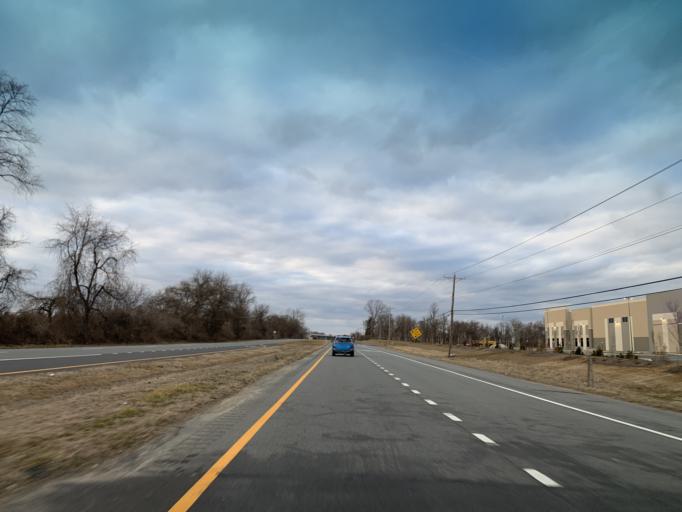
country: US
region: Delaware
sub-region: New Castle County
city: Bear
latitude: 39.5859
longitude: -75.6592
